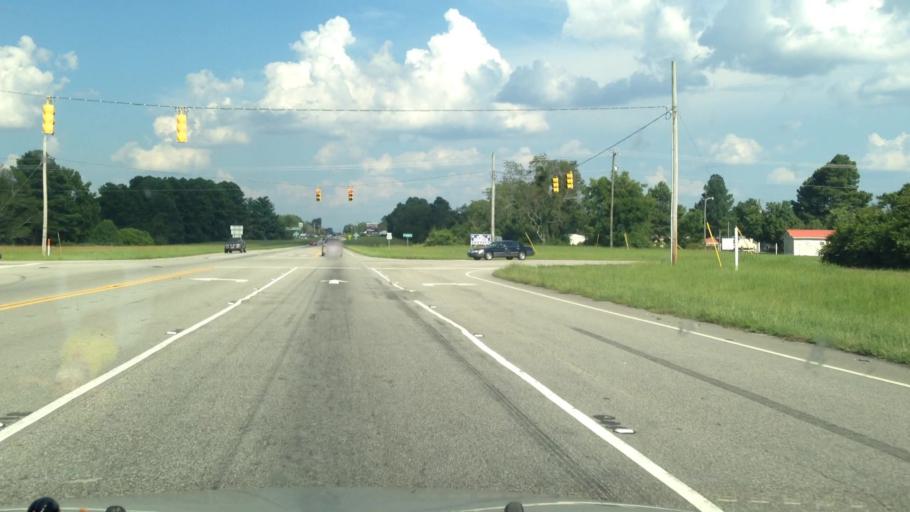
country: US
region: North Carolina
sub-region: Lee County
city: Broadway
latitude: 35.4383
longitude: -79.0369
